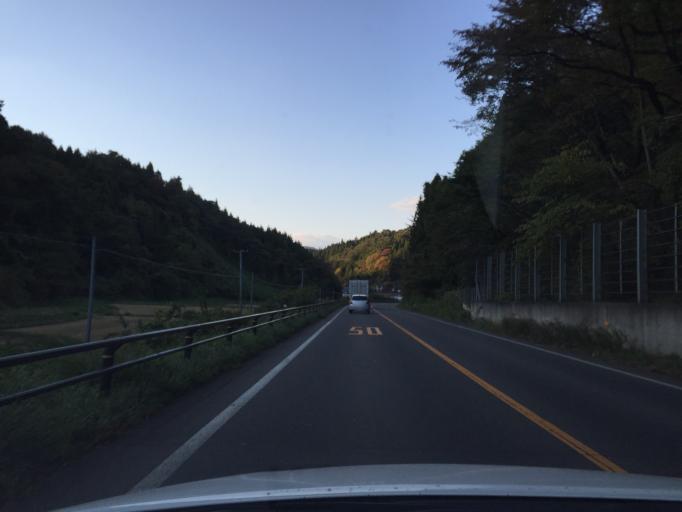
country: JP
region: Fukushima
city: Miharu
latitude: 37.2868
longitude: 140.5431
